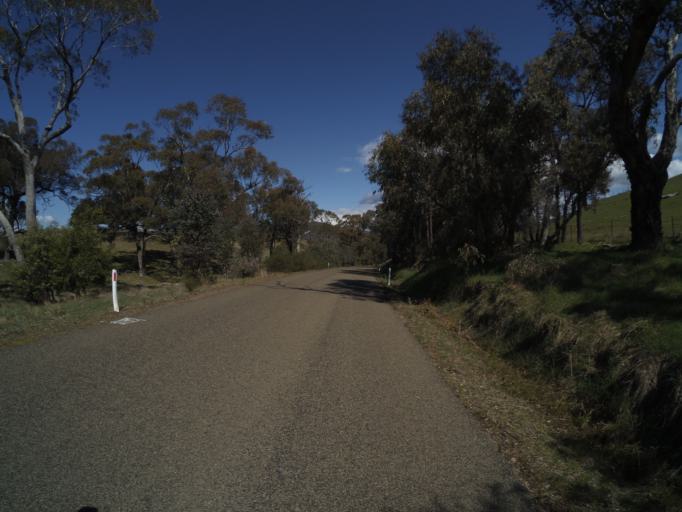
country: AU
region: Australian Capital Territory
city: Macquarie
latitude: -35.1852
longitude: 148.8912
